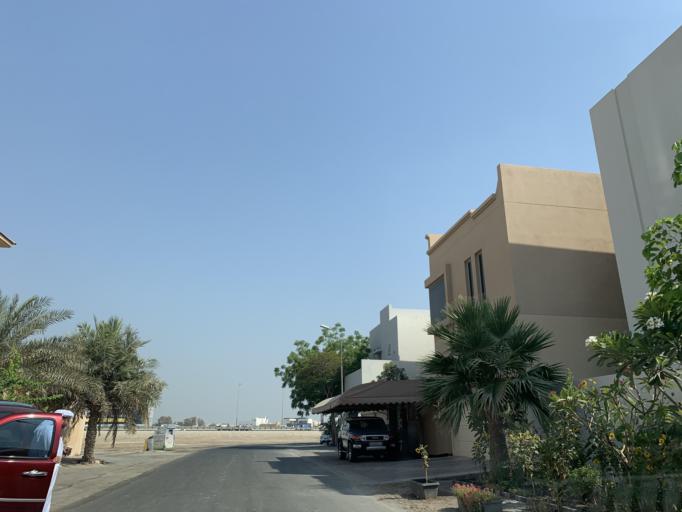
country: BH
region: Northern
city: Madinat `Isa
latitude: 26.1921
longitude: 50.5072
